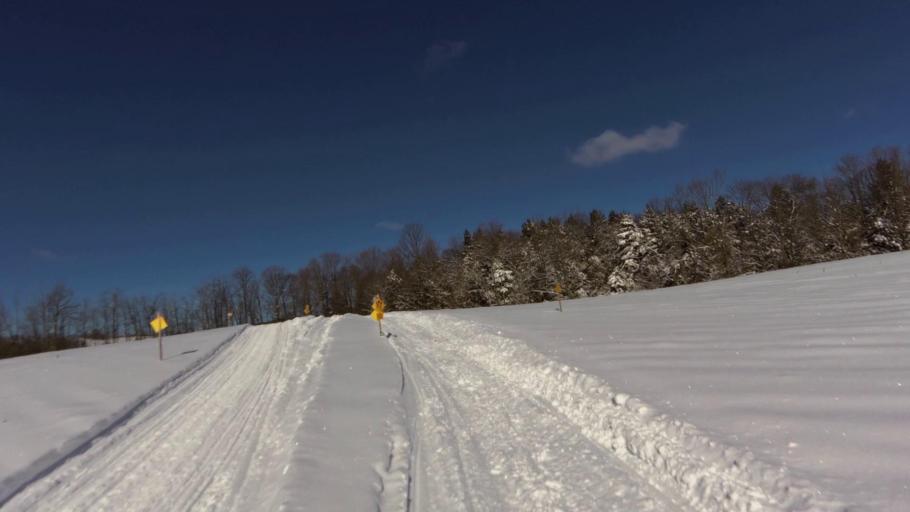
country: US
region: New York
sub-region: Chautauqua County
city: Fredonia
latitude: 42.3544
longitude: -79.1767
